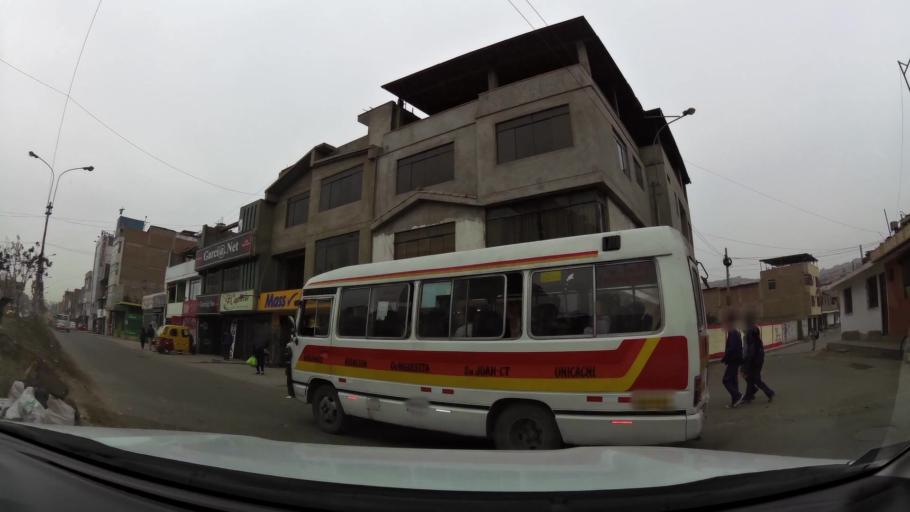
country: PE
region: Lima
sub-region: Lima
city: Surco
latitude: -12.1747
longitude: -76.9671
